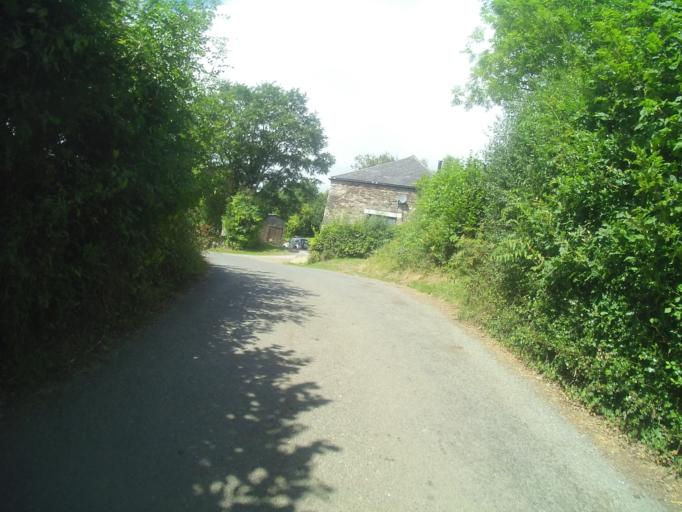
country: GB
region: England
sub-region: Devon
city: Buckfastleigh
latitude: 50.5110
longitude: -3.8235
